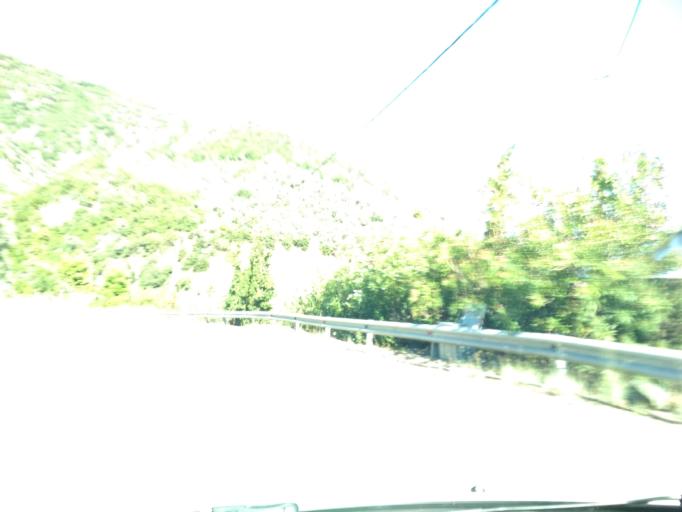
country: GR
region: Central Greece
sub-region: Nomos Evvoias
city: Oreoi
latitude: 38.8423
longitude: 23.0932
